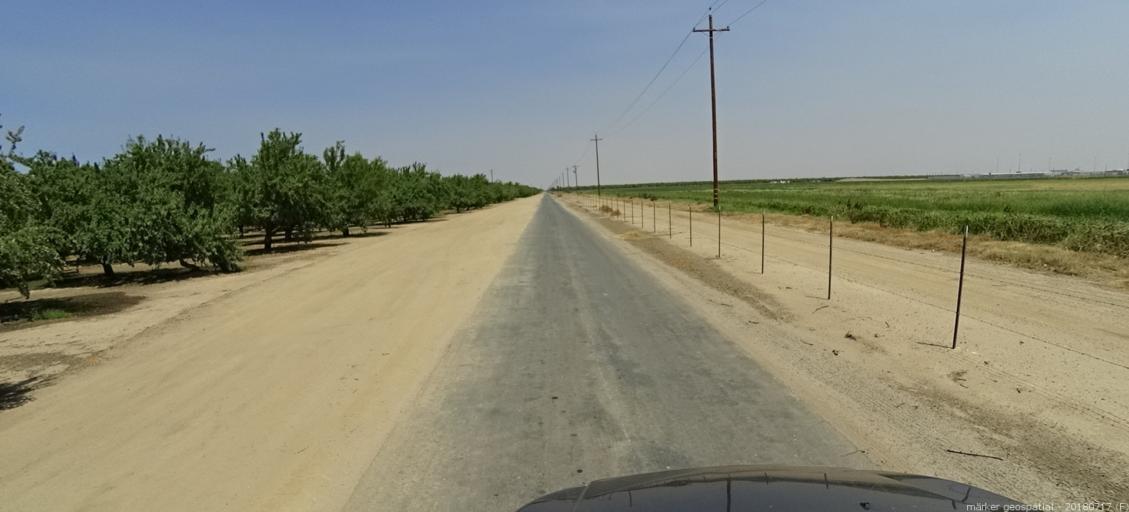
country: US
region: California
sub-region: Madera County
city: Fairmead
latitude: 37.1002
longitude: -120.1659
